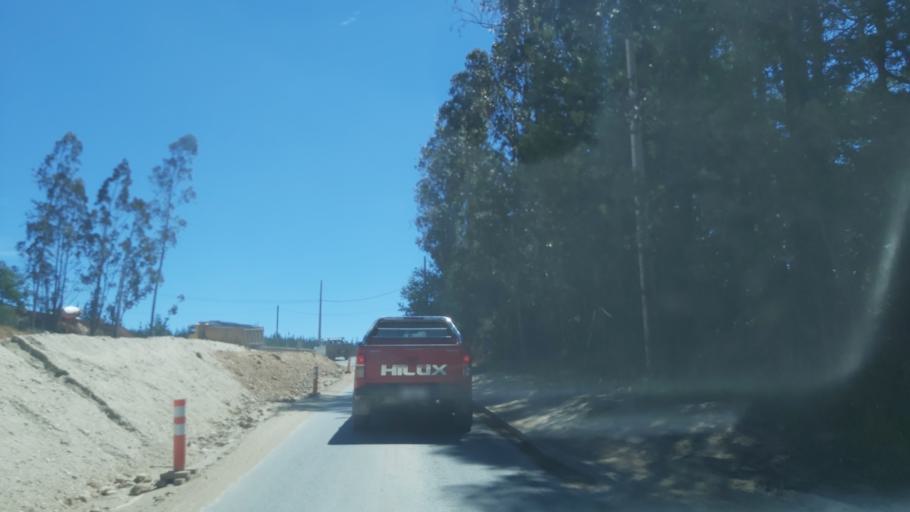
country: CL
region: Maule
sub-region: Provincia de Talca
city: Constitucion
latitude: -35.3868
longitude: -72.4235
